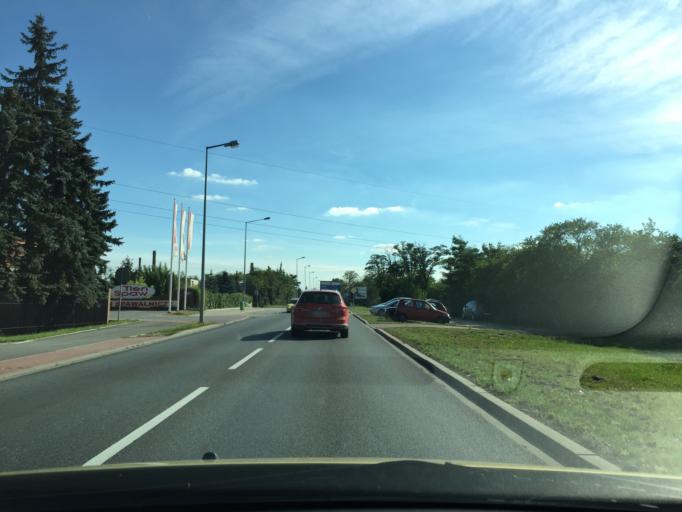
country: PL
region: Greater Poland Voivodeship
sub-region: Kalisz
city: Kalisz
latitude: 51.7897
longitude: 18.0906
